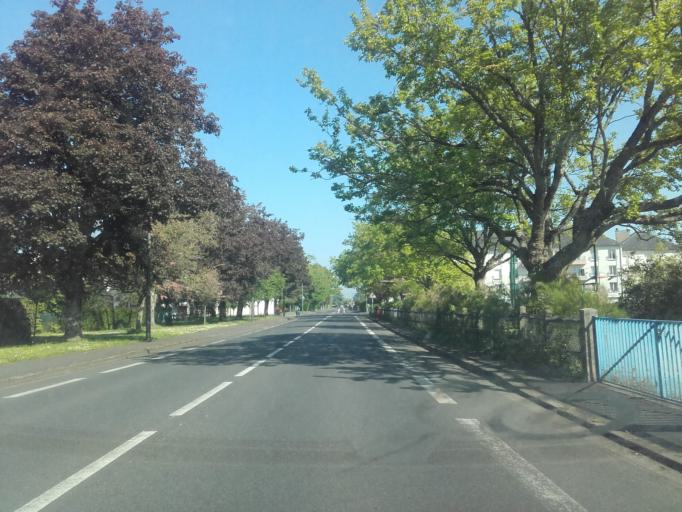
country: FR
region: Centre
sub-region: Departement d'Indre-et-Loire
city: Saint-Cyr-sur-Loire
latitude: 47.4235
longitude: 0.6783
